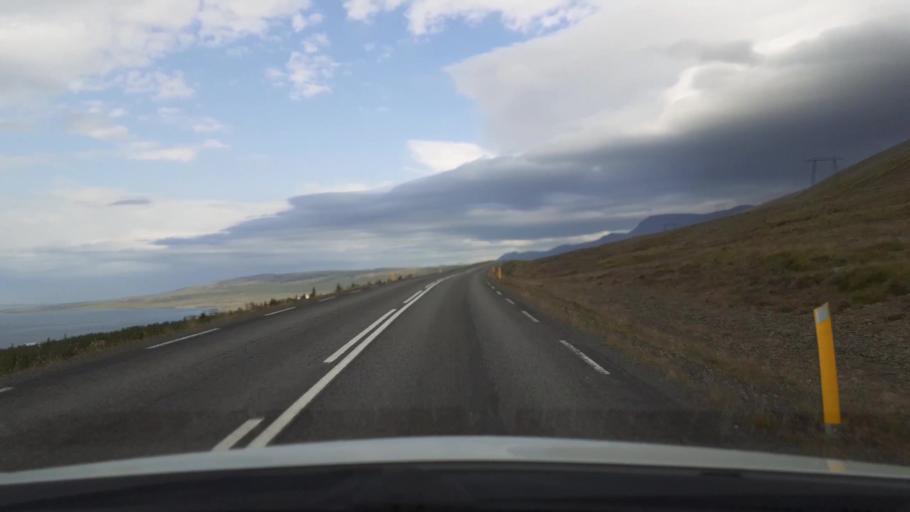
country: IS
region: Capital Region
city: Mosfellsbaer
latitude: 64.4028
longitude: -21.5598
